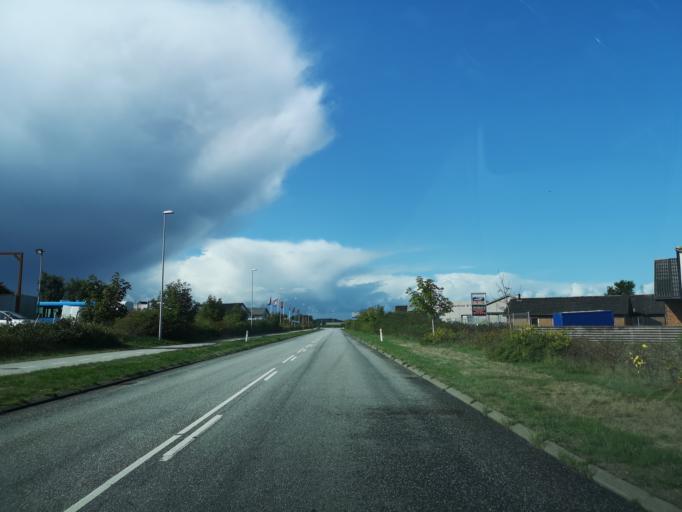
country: DK
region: Central Jutland
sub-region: Herning Kommune
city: Herning
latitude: 56.1330
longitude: 8.9364
